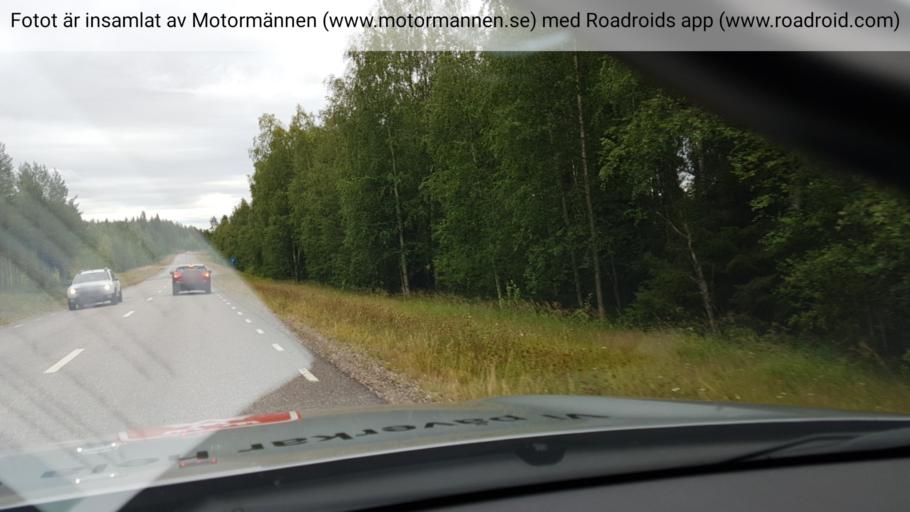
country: SE
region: Norrbotten
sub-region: Overkalix Kommun
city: OEverkalix
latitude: 66.5245
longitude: 22.7611
